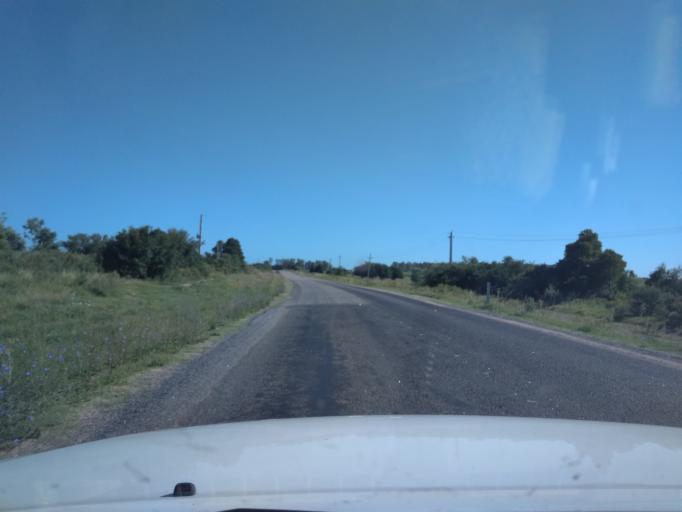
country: UY
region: Canelones
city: San Ramon
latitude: -34.2639
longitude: -55.9279
